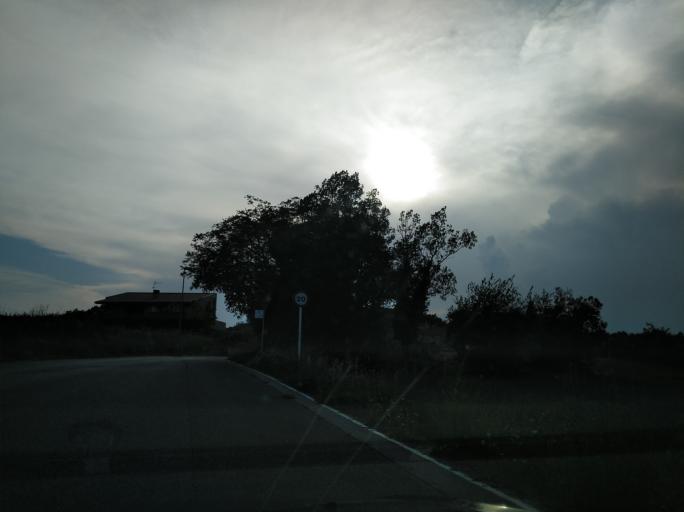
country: ES
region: Catalonia
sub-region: Provincia de Girona
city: Aiguaviva
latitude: 41.9416
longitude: 2.7761
